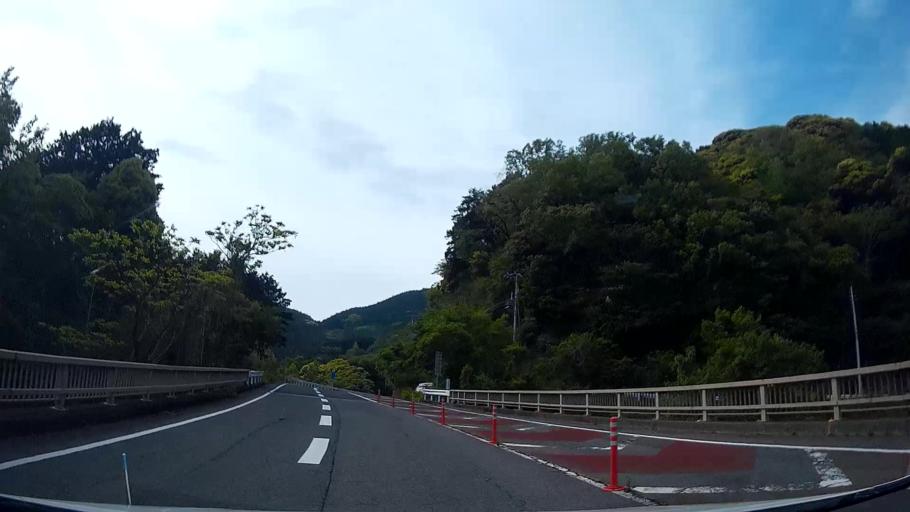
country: JP
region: Shizuoka
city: Heda
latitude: 34.9100
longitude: 138.8172
